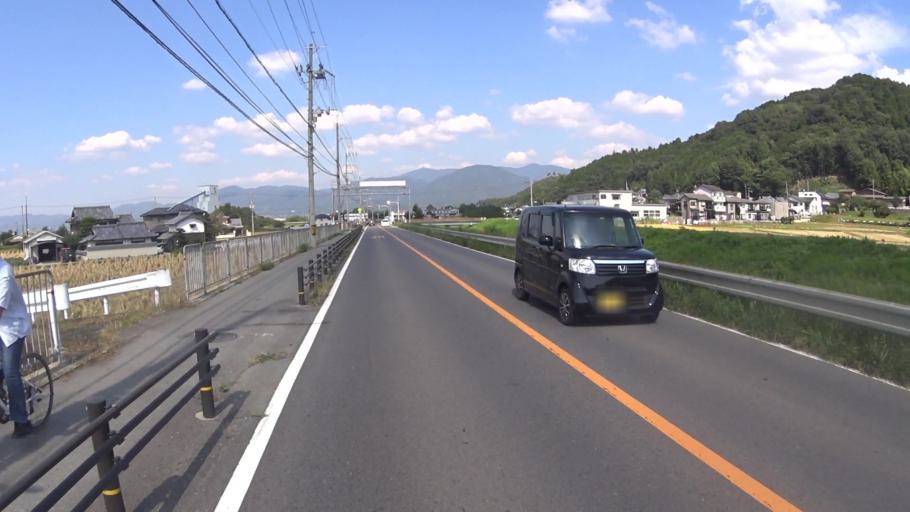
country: JP
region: Kyoto
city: Kameoka
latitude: 35.0027
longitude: 135.5550
